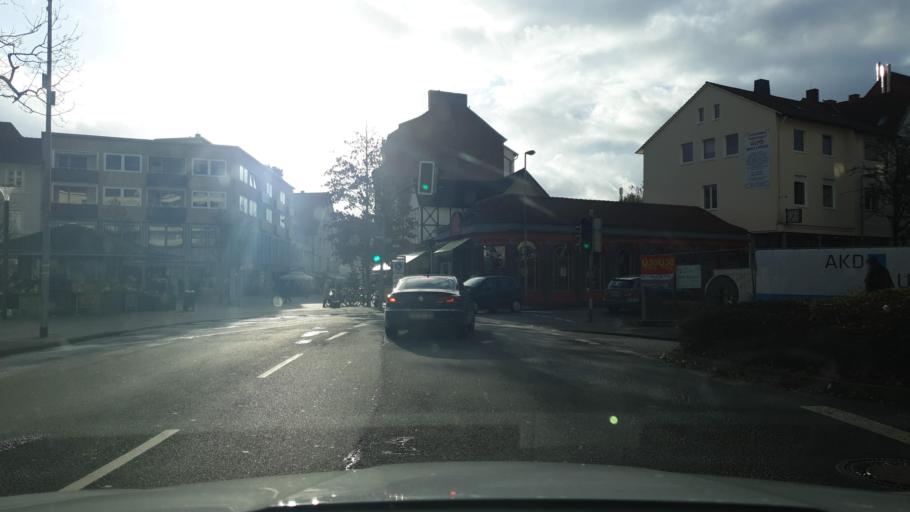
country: DE
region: North Rhine-Westphalia
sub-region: Regierungsbezirk Detmold
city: Bad Salzuflen
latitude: 52.0870
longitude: 8.7454
